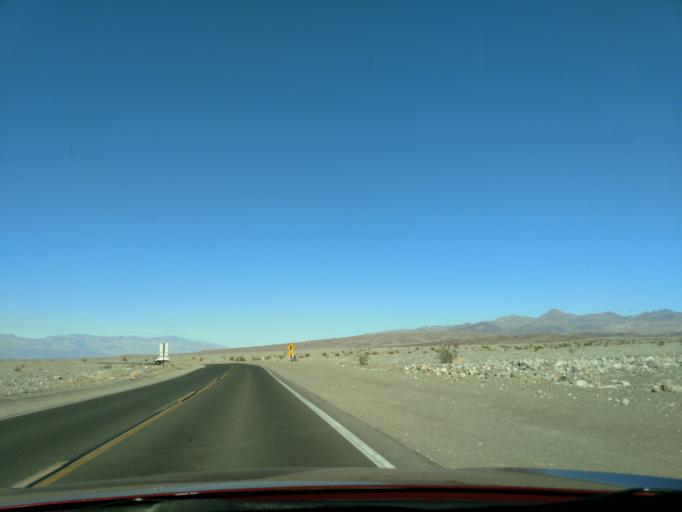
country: US
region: Nevada
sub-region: Nye County
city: Beatty
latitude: 36.5867
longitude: -116.9407
